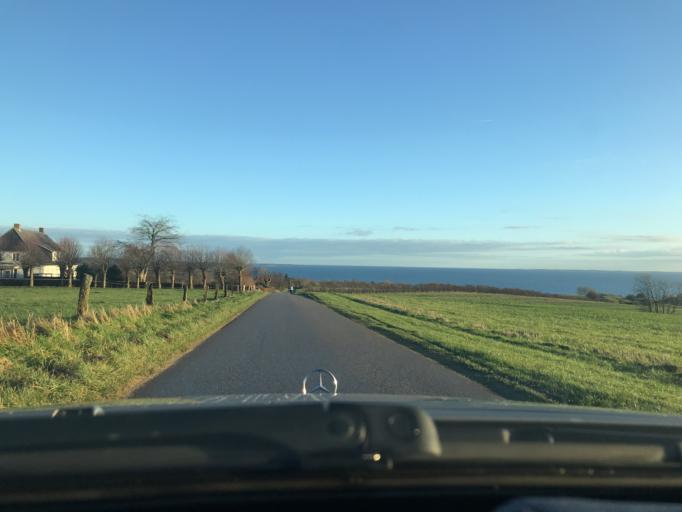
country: DK
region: South Denmark
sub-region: Sonderborg Kommune
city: Dybbol
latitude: 54.9037
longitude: 9.7565
